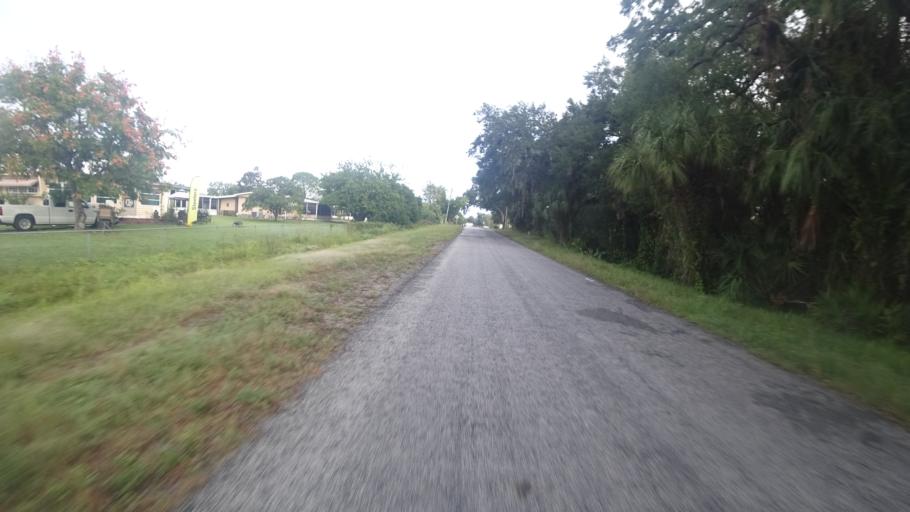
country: US
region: Florida
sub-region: Manatee County
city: Ellenton
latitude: 27.5346
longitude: -82.4828
